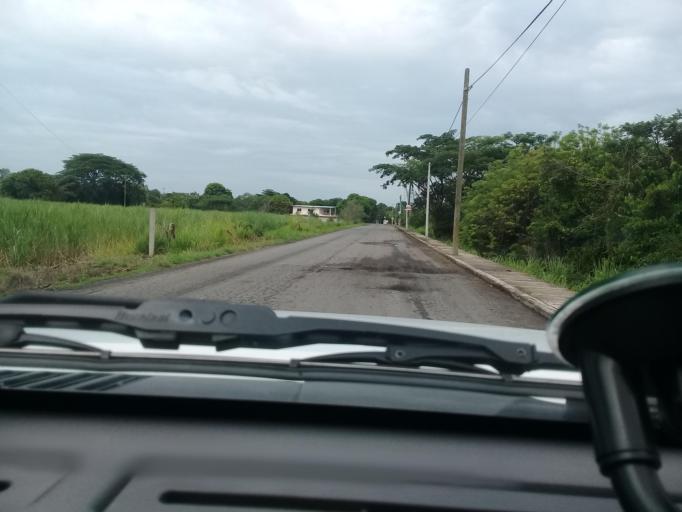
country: MX
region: Veracruz
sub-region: Paso de Ovejas
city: El Hatito
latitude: 19.3162
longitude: -96.3800
